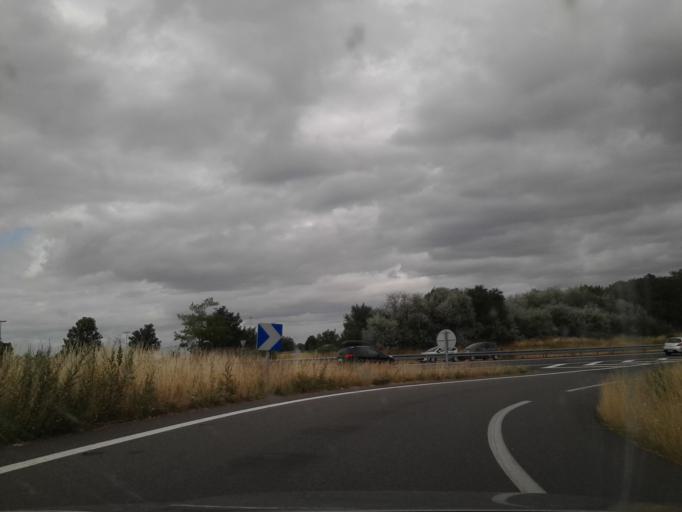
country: FR
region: Centre
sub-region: Departement du Cher
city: La Chapelle-Saint-Ursin
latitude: 47.0429
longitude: 2.3379
